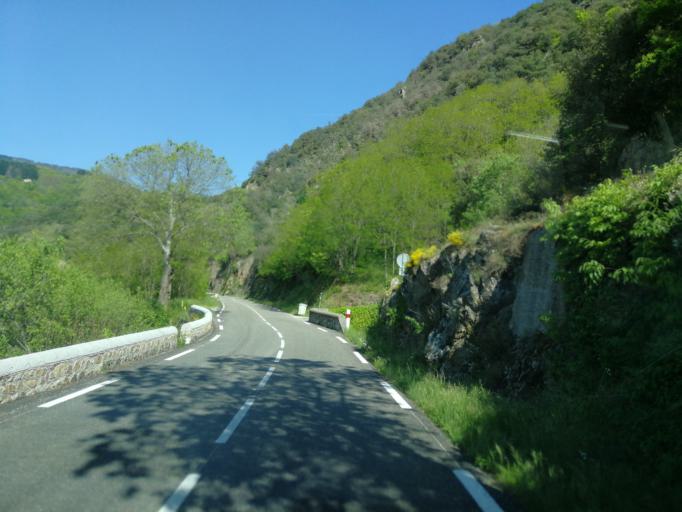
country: FR
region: Rhone-Alpes
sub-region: Departement de l'Ardeche
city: Saint-Sauveur-de-Montagut
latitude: 44.8525
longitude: 4.5707
